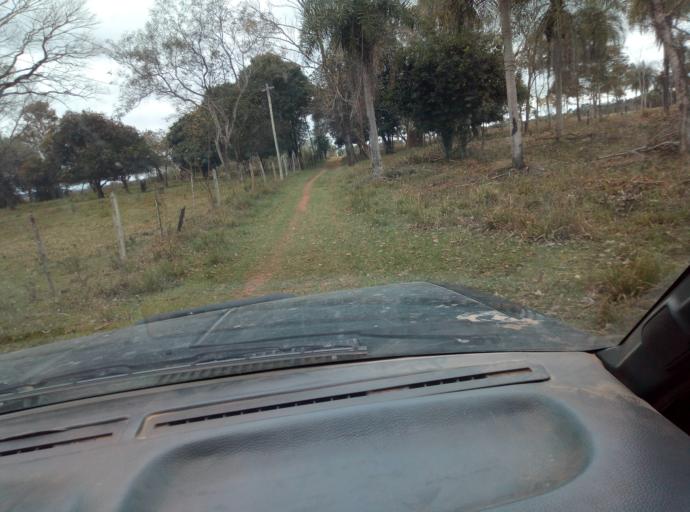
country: PY
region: Caaguazu
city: Doctor Cecilio Baez
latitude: -25.1443
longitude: -56.2983
